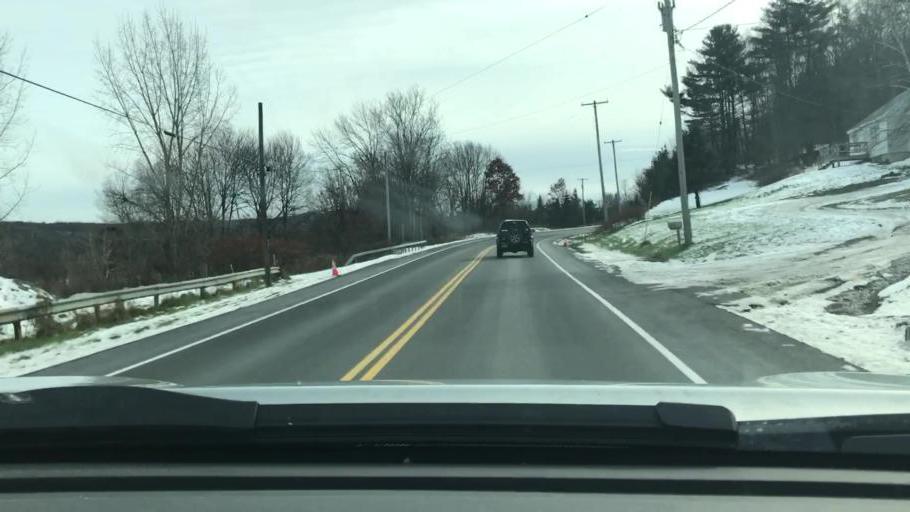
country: US
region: Vermont
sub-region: Rutland County
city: Poultney
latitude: 43.5324
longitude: -73.2496
